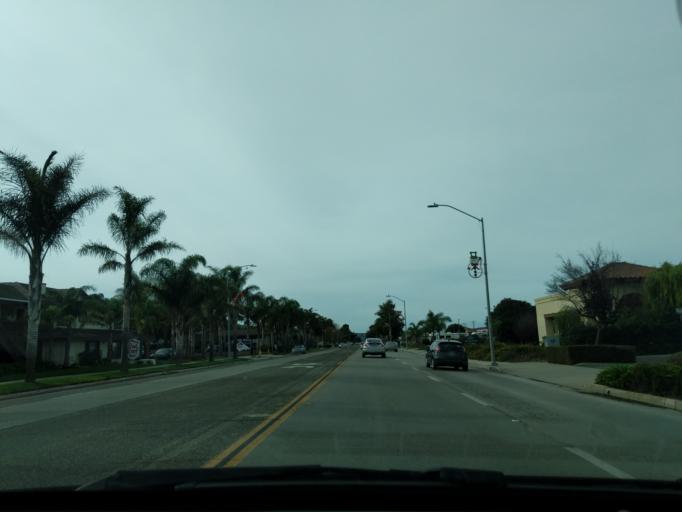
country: US
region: California
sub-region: Santa Barbara County
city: Lompoc
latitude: 34.6389
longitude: -120.4454
